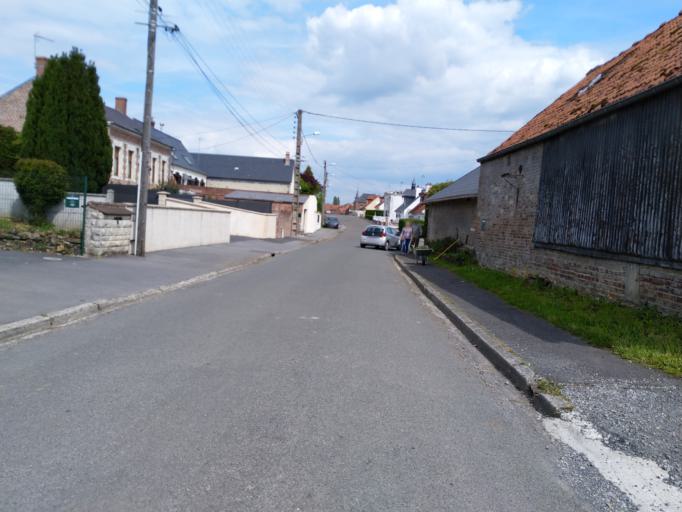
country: FR
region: Picardie
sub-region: Departement de l'Aisne
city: Boue
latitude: 50.0128
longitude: 3.6947
